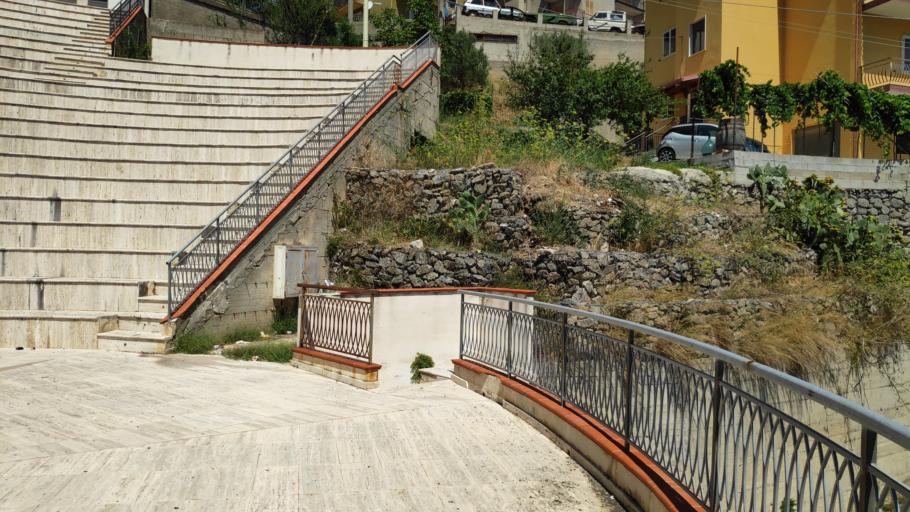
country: IT
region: Calabria
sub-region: Provincia di Catanzaro
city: Gasperina
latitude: 38.7390
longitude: 16.5096
